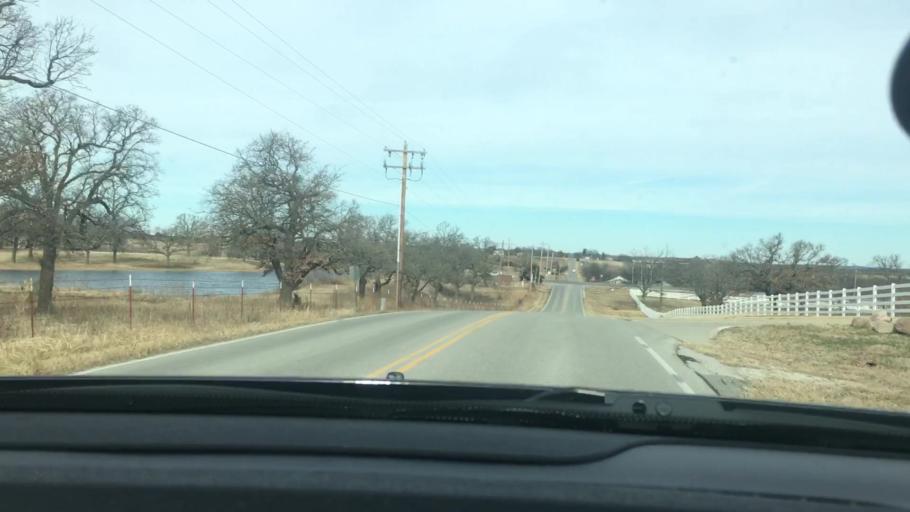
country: US
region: Oklahoma
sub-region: Carter County
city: Ardmore
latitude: 34.1846
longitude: -97.0731
